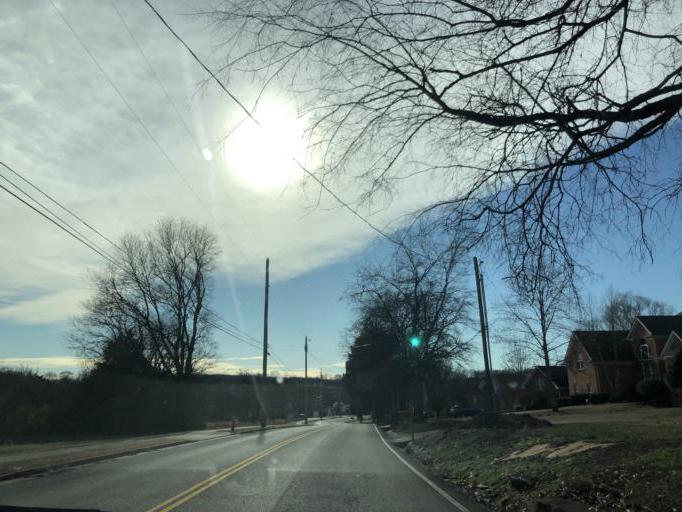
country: US
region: Tennessee
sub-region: Wilson County
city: Green Hill
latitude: 36.1568
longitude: -86.5837
